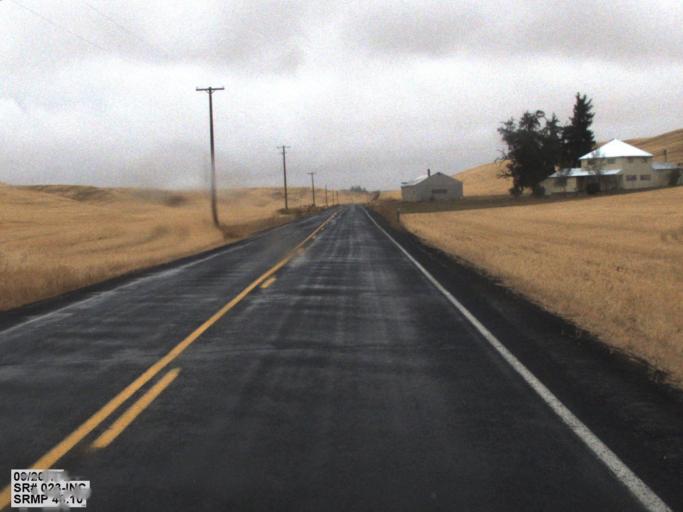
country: US
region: Washington
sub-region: Lincoln County
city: Davenport
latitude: 47.3491
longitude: -118.0238
